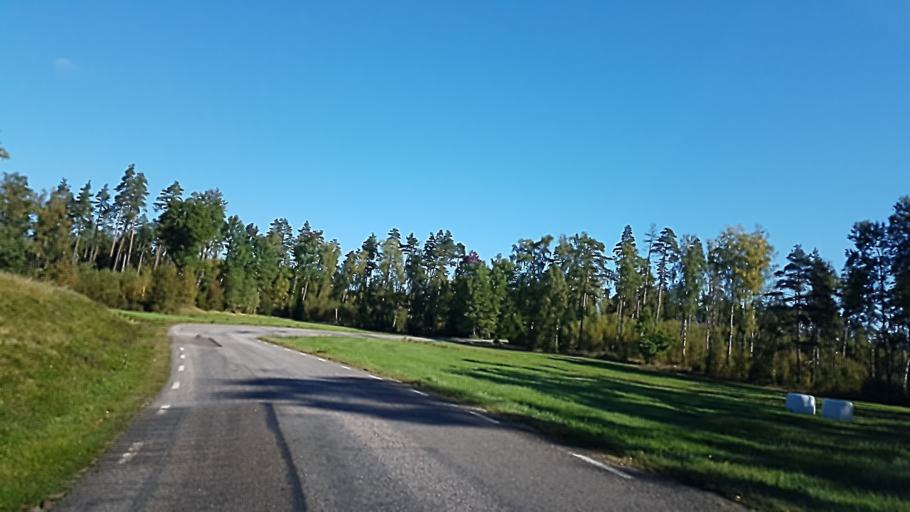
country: SE
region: Kronoberg
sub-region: Ljungby Kommun
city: Ljungby
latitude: 56.8146
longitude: 14.0366
